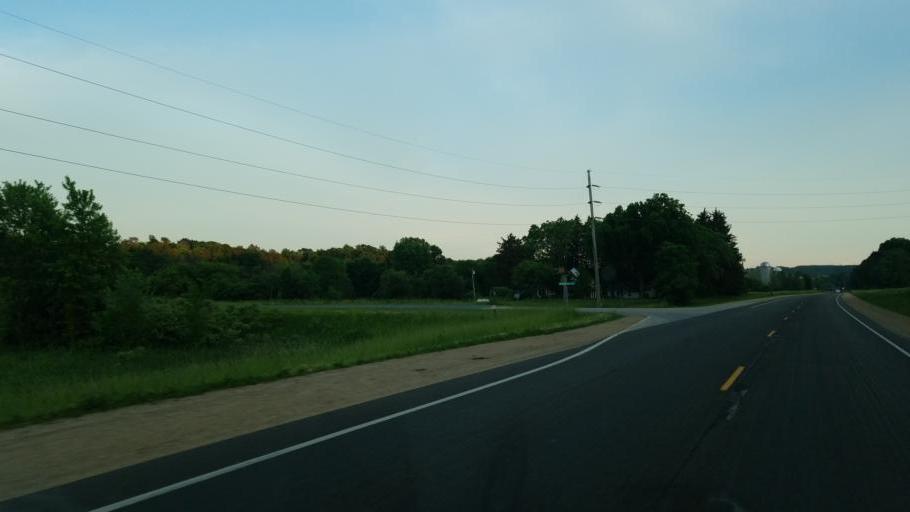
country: US
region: Wisconsin
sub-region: Monroe County
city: Tomah
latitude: 43.9371
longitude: -90.5029
